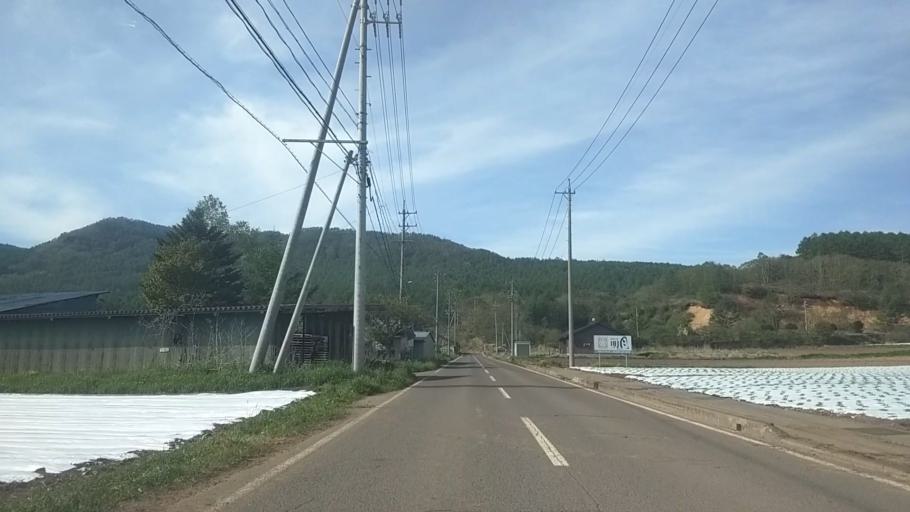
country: JP
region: Yamanashi
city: Nirasaki
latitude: 35.9391
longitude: 138.4660
